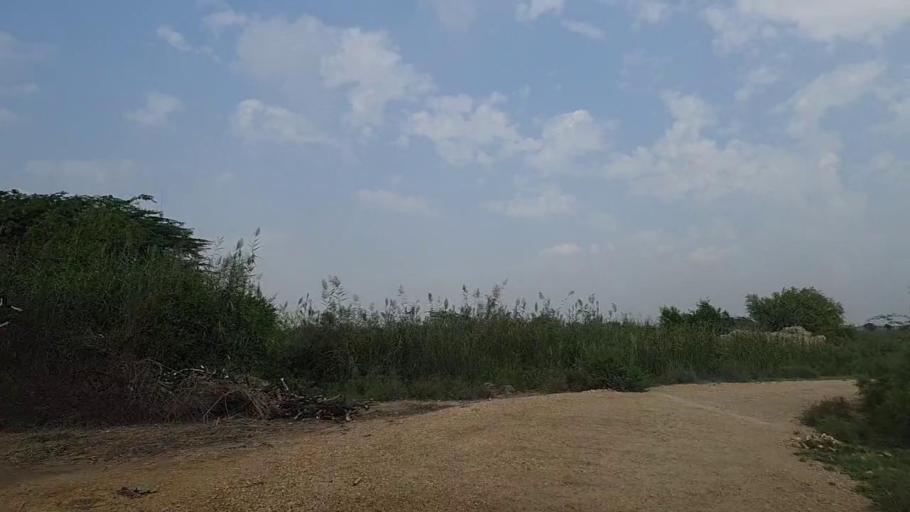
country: PK
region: Sindh
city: Daro Mehar
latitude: 24.6958
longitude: 68.1199
